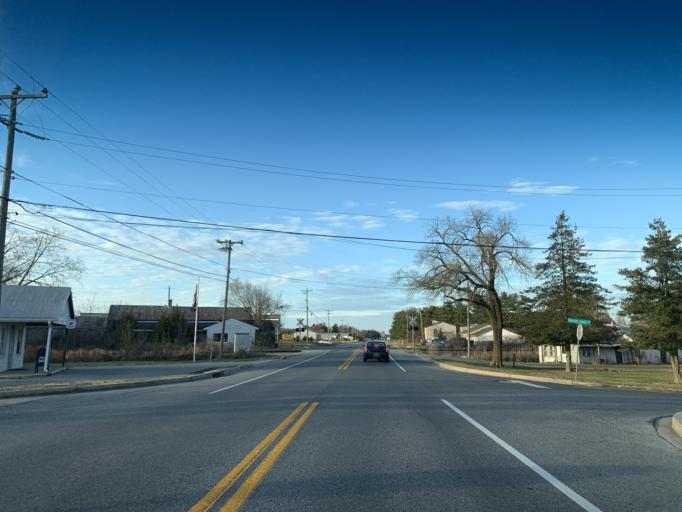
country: US
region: Maryland
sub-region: Kent County
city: Chestertown
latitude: 39.2742
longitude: -76.0919
